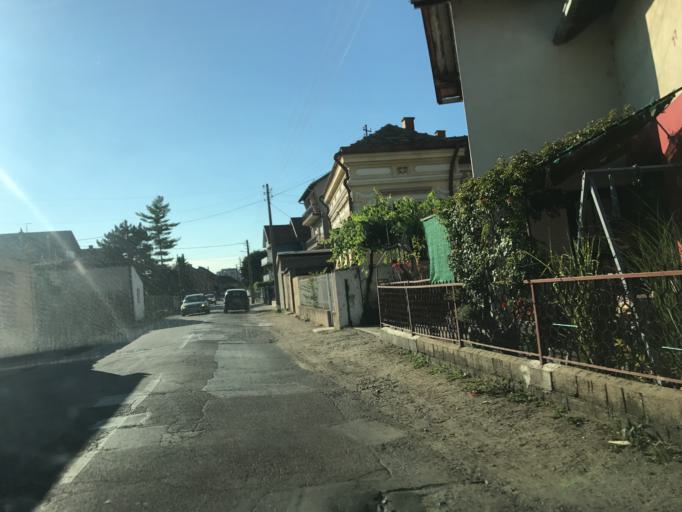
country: RS
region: Central Serbia
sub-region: Borski Okrug
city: Negotin
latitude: 44.2260
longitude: 22.5379
